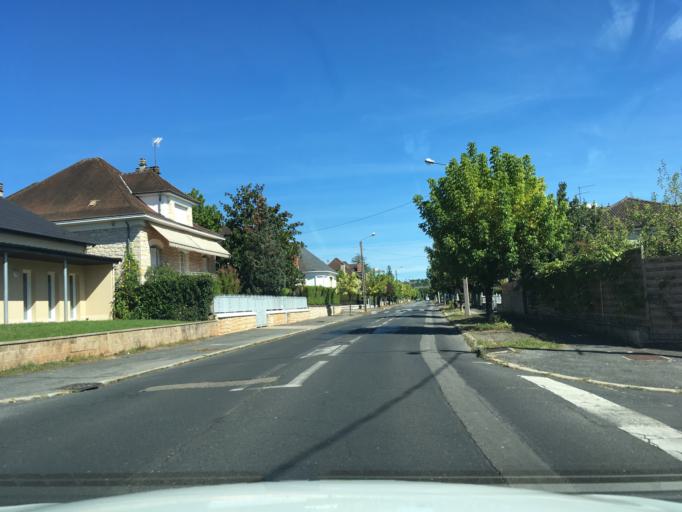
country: FR
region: Limousin
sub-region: Departement de la Correze
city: Brive-la-Gaillarde
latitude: 45.1667
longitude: 1.5222
